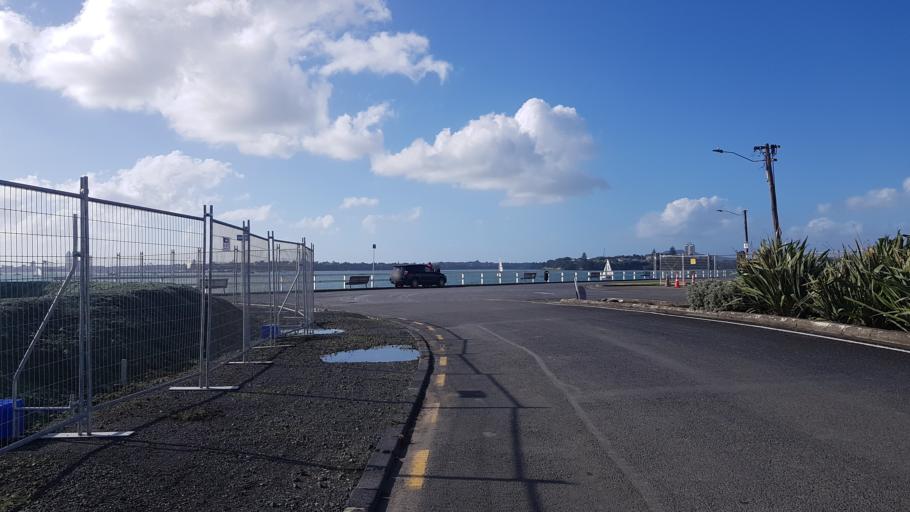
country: NZ
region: Auckland
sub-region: Auckland
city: Auckland
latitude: -36.8370
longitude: 174.7580
